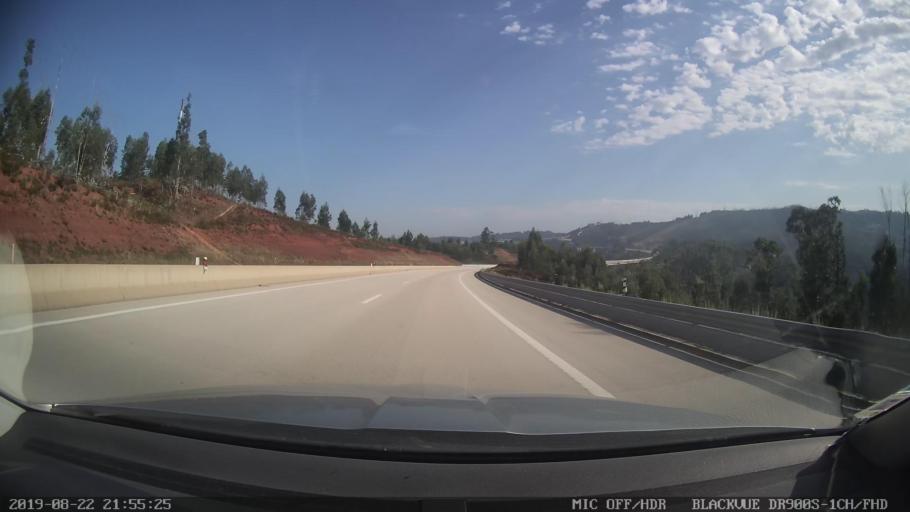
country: PT
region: Coimbra
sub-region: Coimbra
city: Coimbra
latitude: 40.1531
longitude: -8.3848
